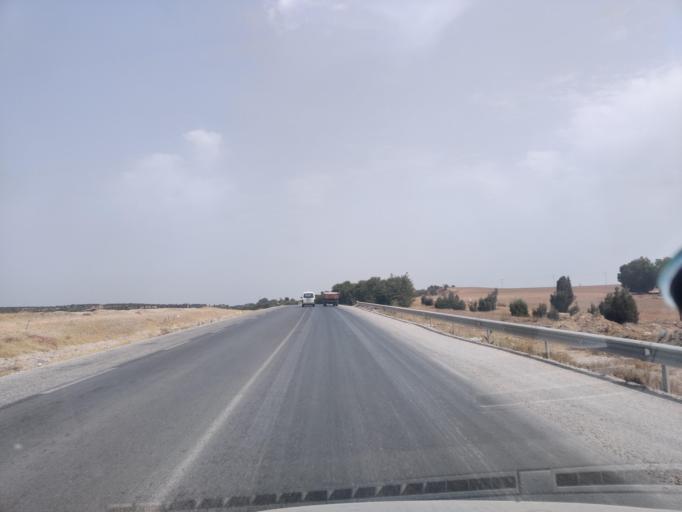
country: TN
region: Nabul
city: Bu `Urqub
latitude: 36.4664
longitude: 10.5719
